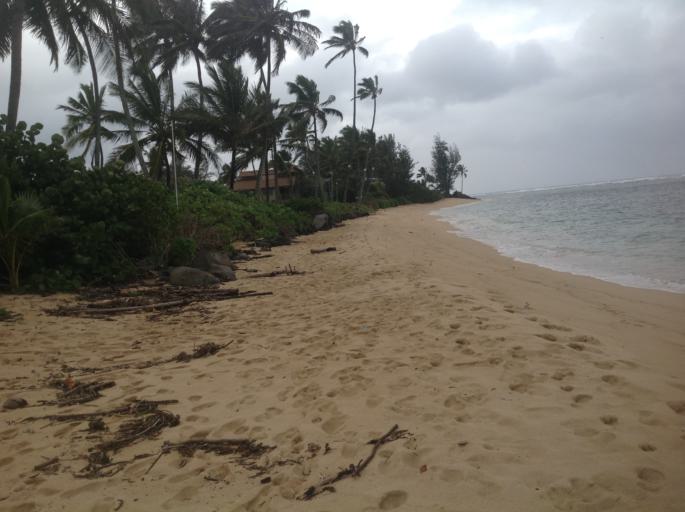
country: US
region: Hawaii
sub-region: Honolulu County
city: Waialua
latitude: 21.5825
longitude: -158.1329
